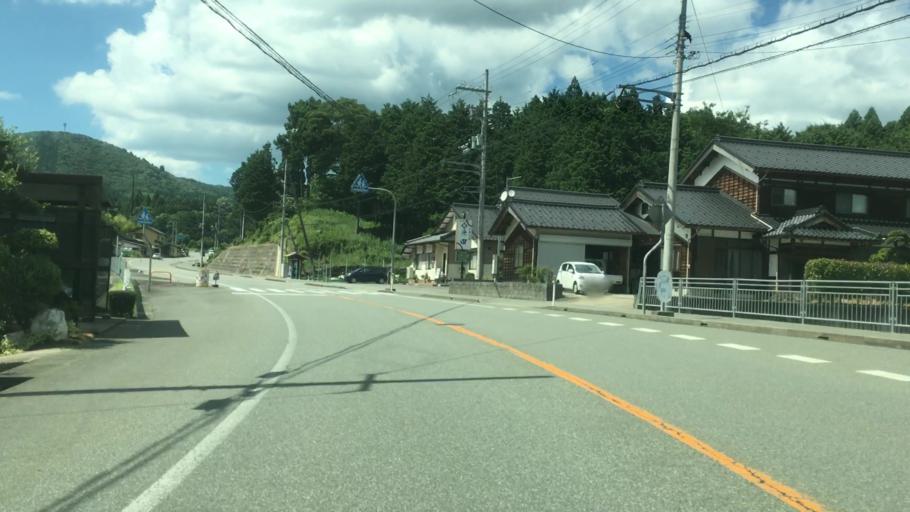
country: JP
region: Hyogo
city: Toyooka
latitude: 35.4808
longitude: 134.7085
